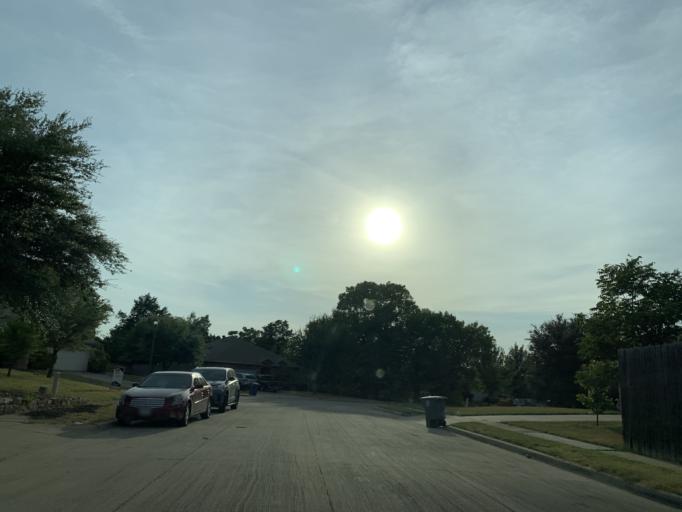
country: US
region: Texas
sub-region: Dallas County
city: Cockrell Hill
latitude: 32.6986
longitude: -96.8947
